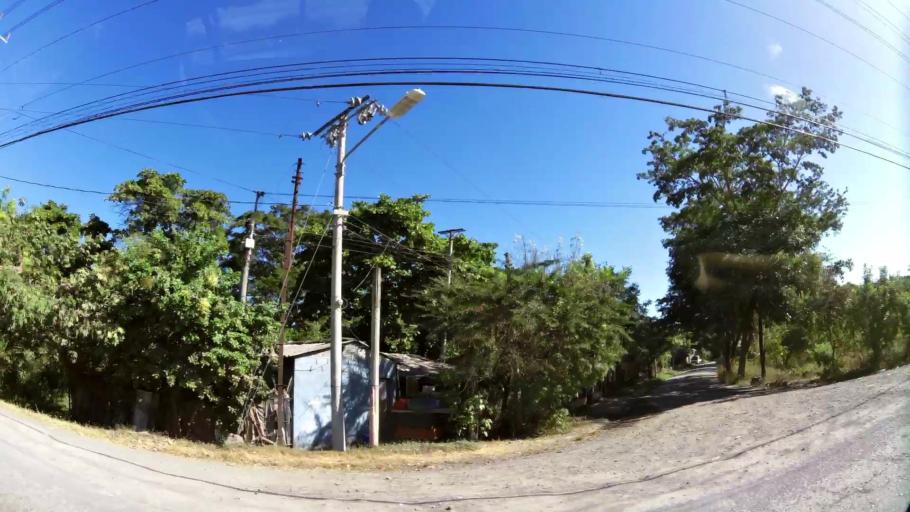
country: SV
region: San Miguel
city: San Miguel
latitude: 13.4604
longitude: -88.1486
